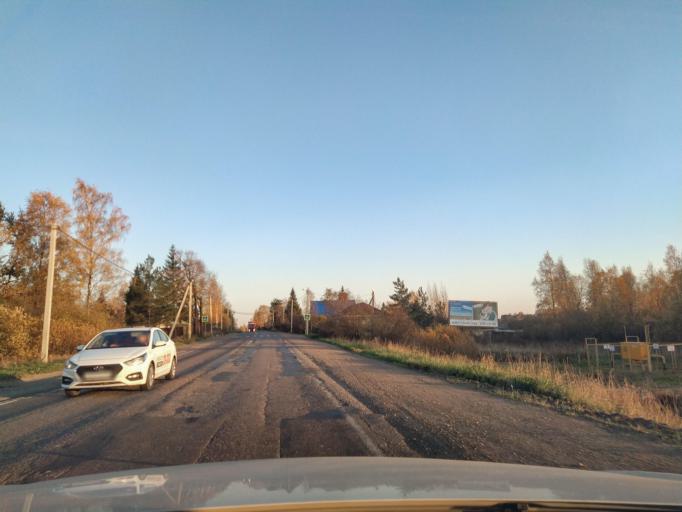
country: RU
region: Leningrad
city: Maloye Verevo
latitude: 59.6147
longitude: 30.2183
